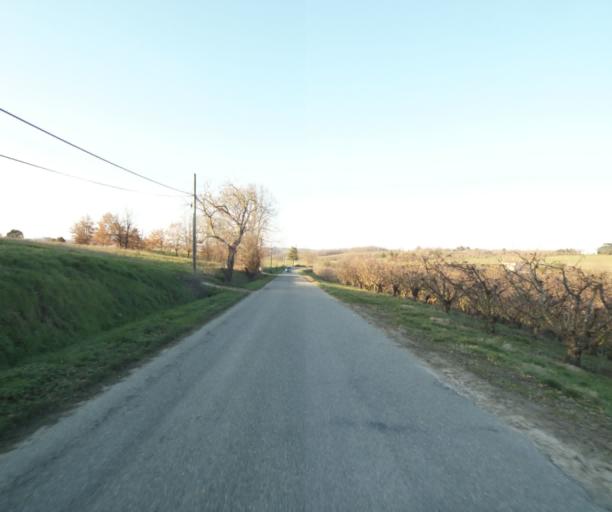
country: FR
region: Midi-Pyrenees
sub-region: Departement du Tarn-et-Garonne
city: Moissac
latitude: 44.1290
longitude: 1.1216
